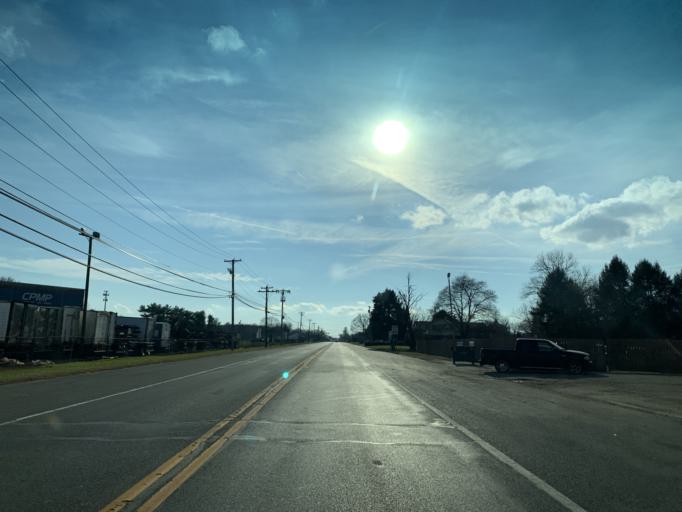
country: US
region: New Jersey
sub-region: Salem County
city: Penns Grove
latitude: 39.7442
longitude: -75.4545
